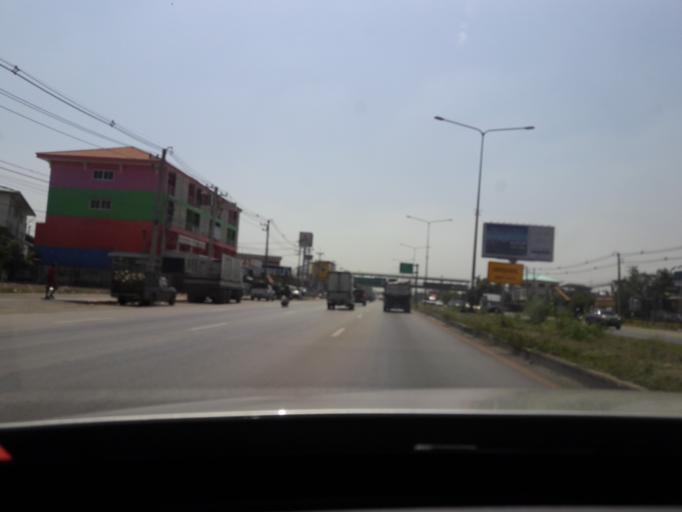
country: TH
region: Bangkok
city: Nong Khaem
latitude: 13.6770
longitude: 100.3197
